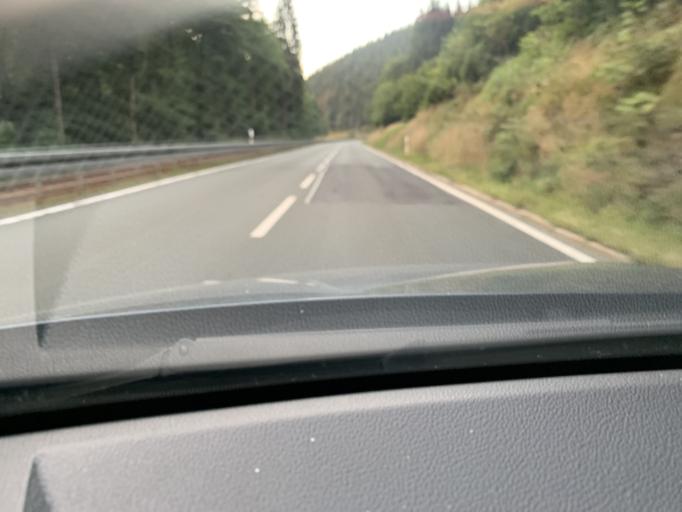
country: DE
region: Thuringia
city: Steinach
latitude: 50.4112
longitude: 11.1807
